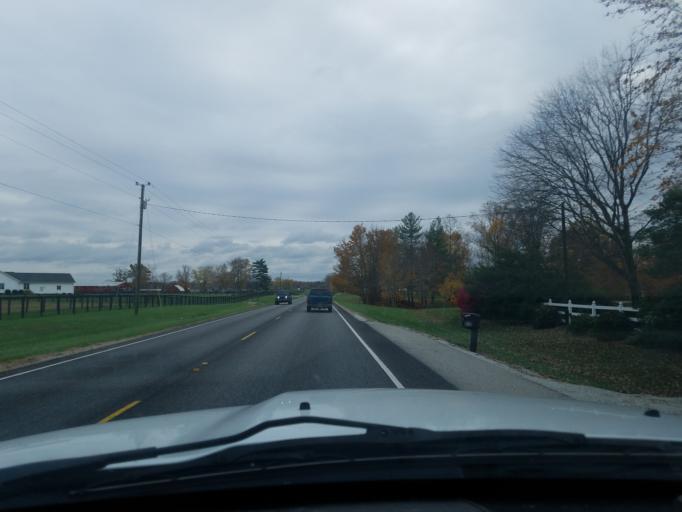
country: US
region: Indiana
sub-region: Jackson County
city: Crothersville
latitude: 38.8839
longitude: -85.8187
